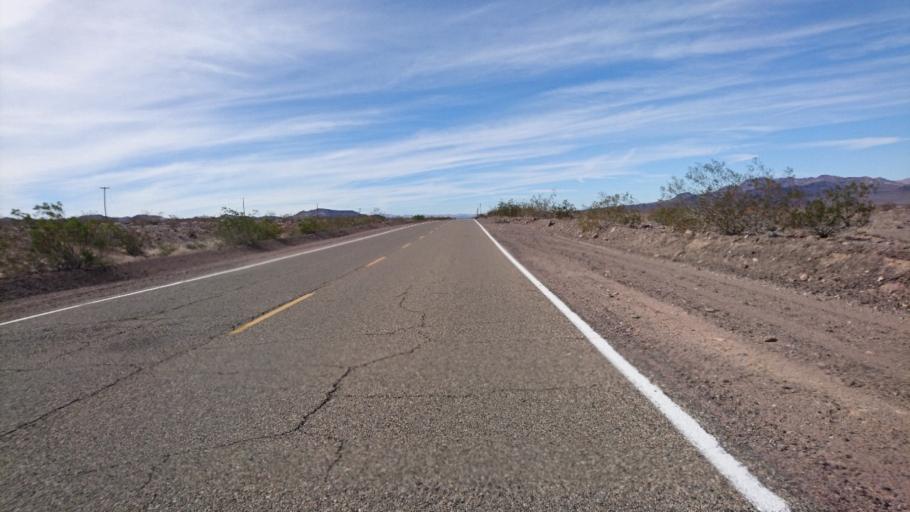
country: US
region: California
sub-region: San Bernardino County
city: Twentynine Palms
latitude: 34.7246
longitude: -116.1371
